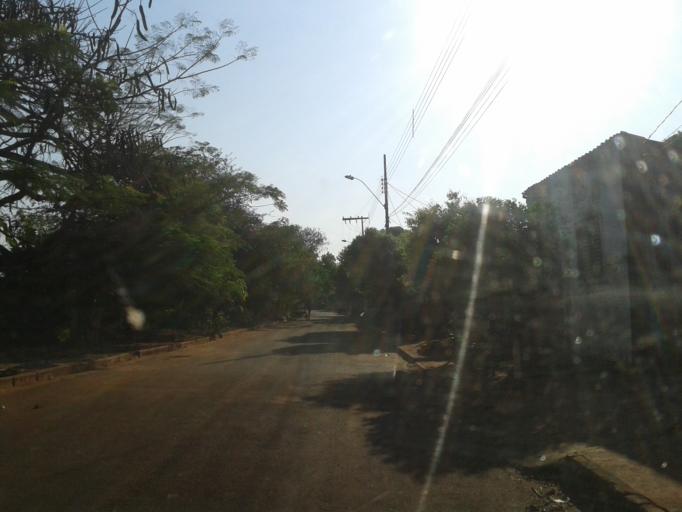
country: BR
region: Minas Gerais
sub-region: Ituiutaba
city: Ituiutaba
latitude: -18.9626
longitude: -49.4731
